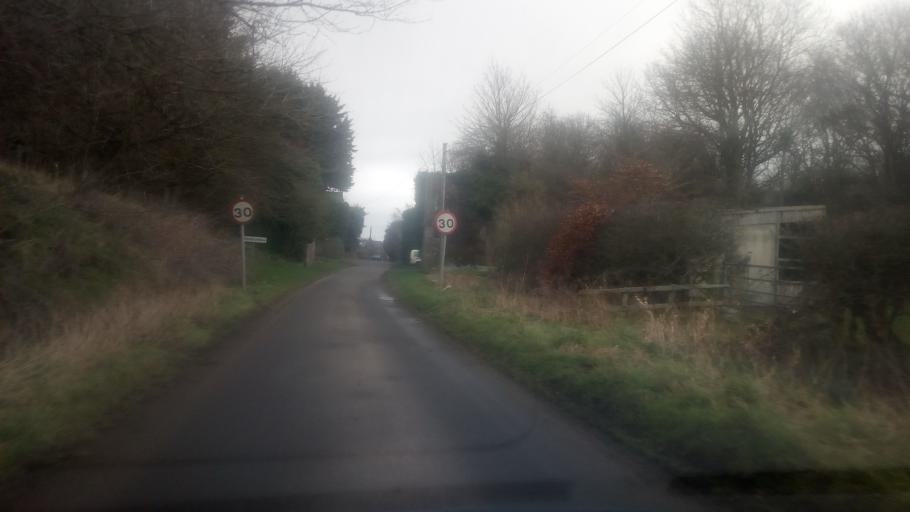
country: GB
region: Scotland
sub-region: The Scottish Borders
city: Kelso
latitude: 55.5669
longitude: -2.4817
